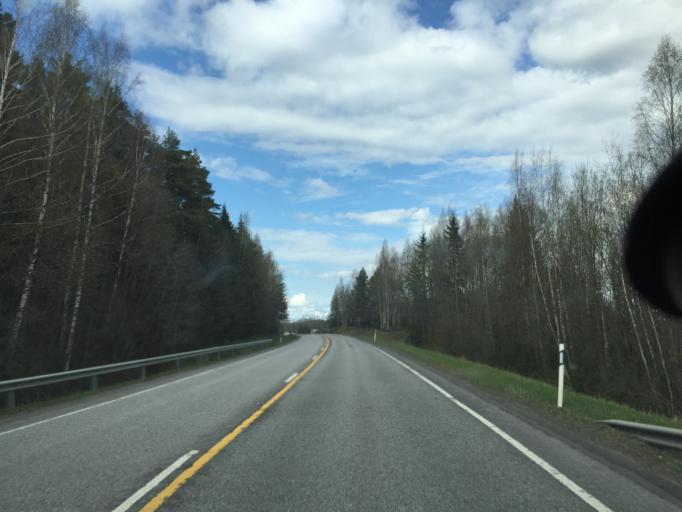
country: FI
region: Uusimaa
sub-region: Helsinki
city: Lohja
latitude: 60.1839
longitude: 24.0069
